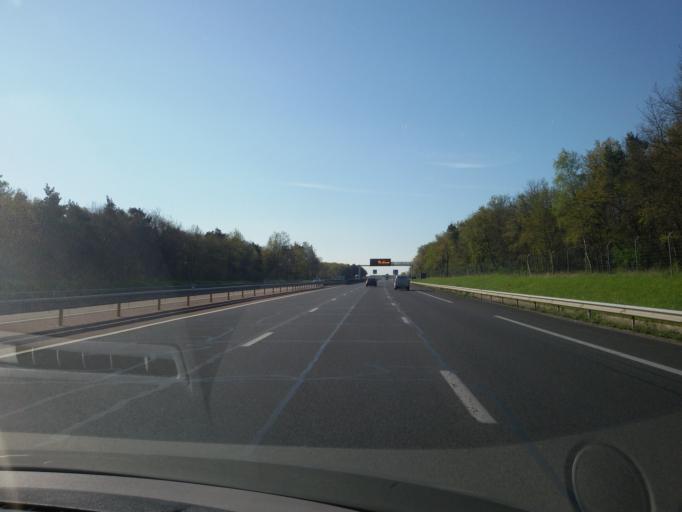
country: FR
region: Ile-de-France
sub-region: Departement de Seine-et-Marne
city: Bagneaux-sur-Loing
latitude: 48.2383
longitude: 2.7519
